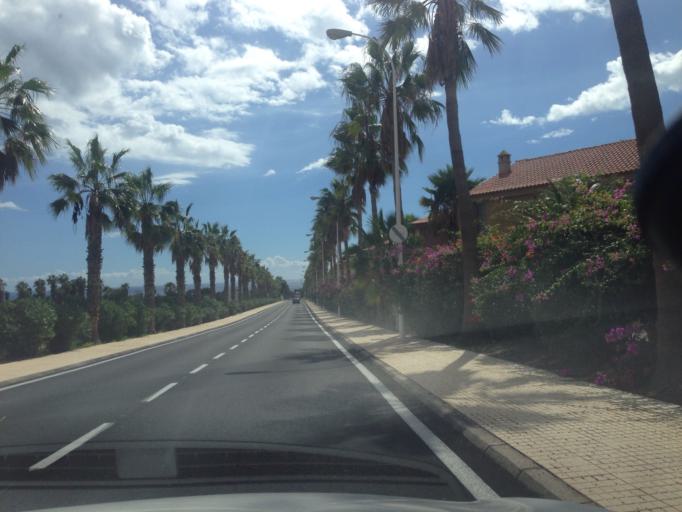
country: ES
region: Canary Islands
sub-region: Provincia de Santa Cruz de Tenerife
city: Las Rosas
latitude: 28.0423
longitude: -16.6121
